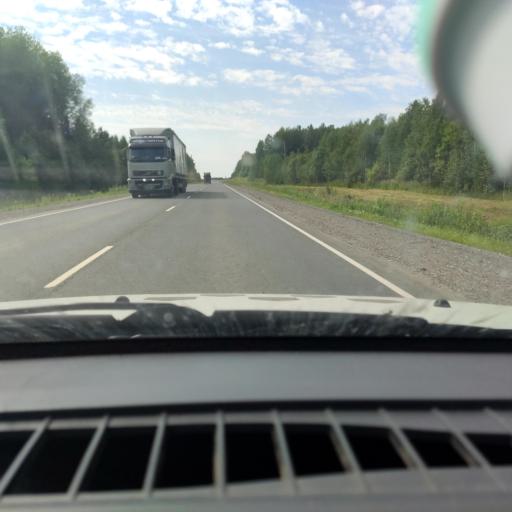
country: RU
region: Kirov
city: Kostino
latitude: 58.8317
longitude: 53.5156
